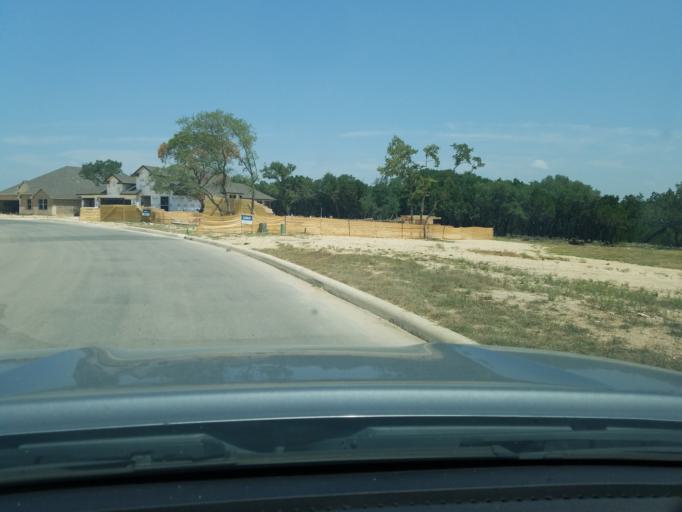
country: US
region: Texas
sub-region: Bexar County
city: Timberwood Park
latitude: 29.7119
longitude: -98.5061
